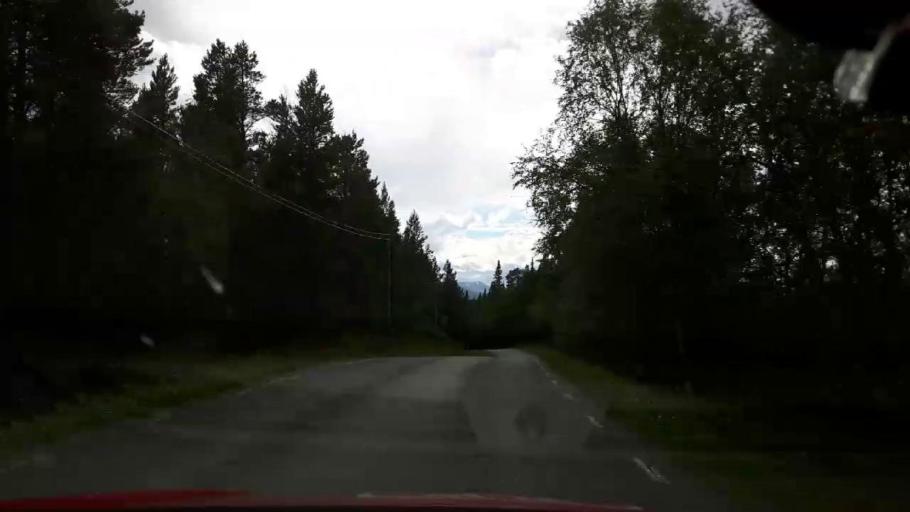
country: SE
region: Jaemtland
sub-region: Are Kommun
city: Are
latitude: 63.1521
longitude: 13.0033
